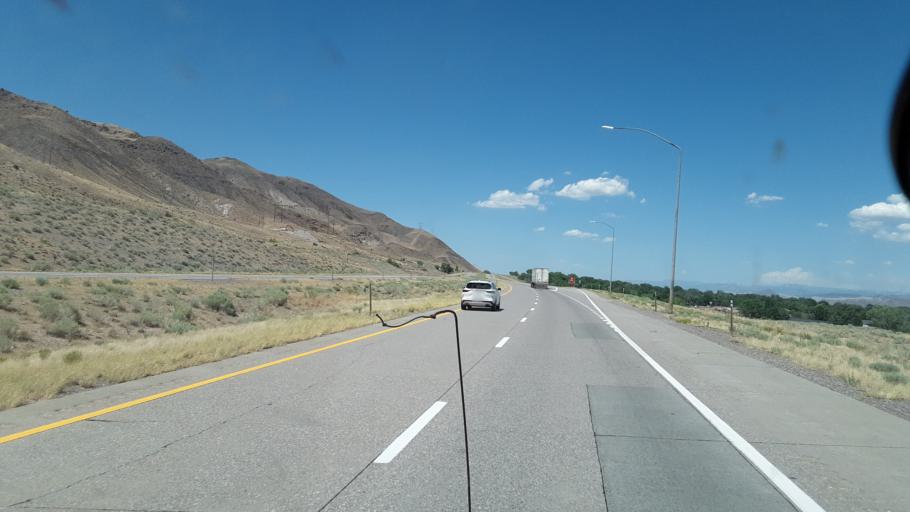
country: US
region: Utah
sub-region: Sevier County
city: Monroe
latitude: 38.6745
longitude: -112.1611
